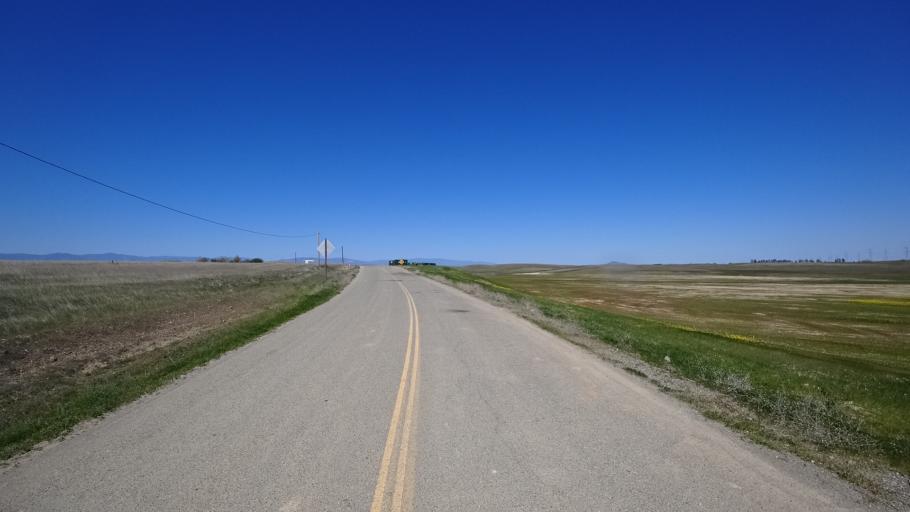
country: US
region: California
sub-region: Glenn County
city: Willows
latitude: 39.6322
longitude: -122.2780
